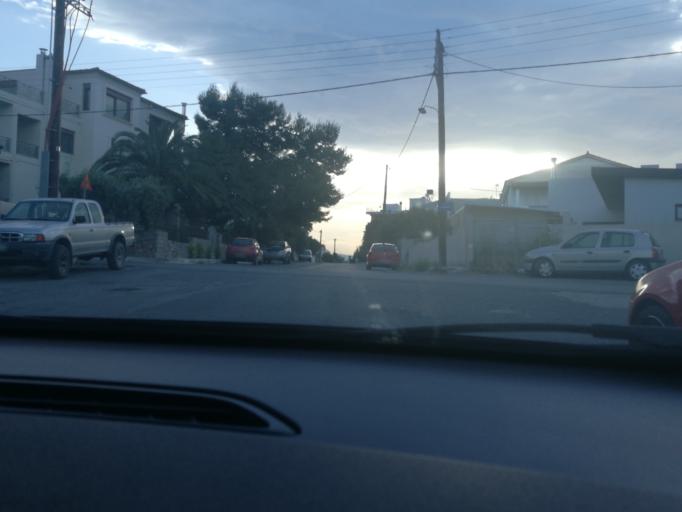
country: GR
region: Crete
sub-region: Nomos Irakleiou
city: Irakleion
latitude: 35.3188
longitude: 25.1483
